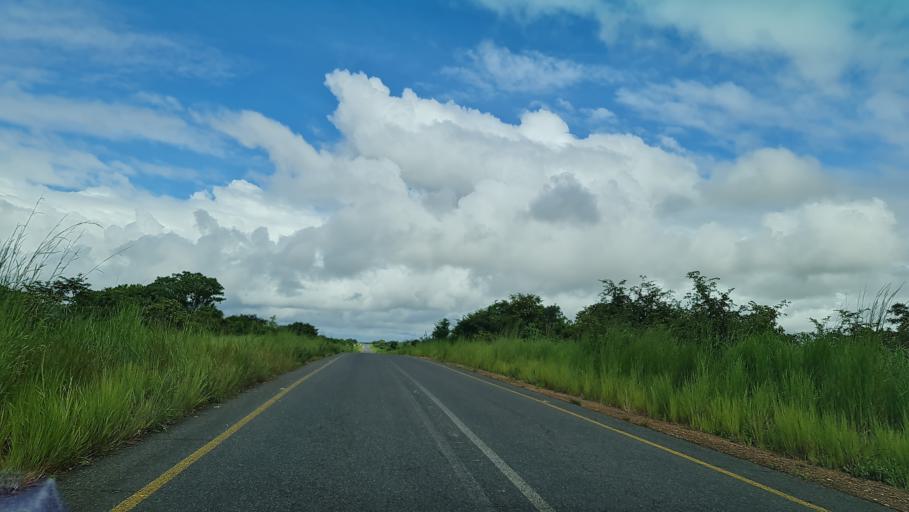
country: MZ
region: Nampula
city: Nampula
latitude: -15.0227
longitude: 38.4877
